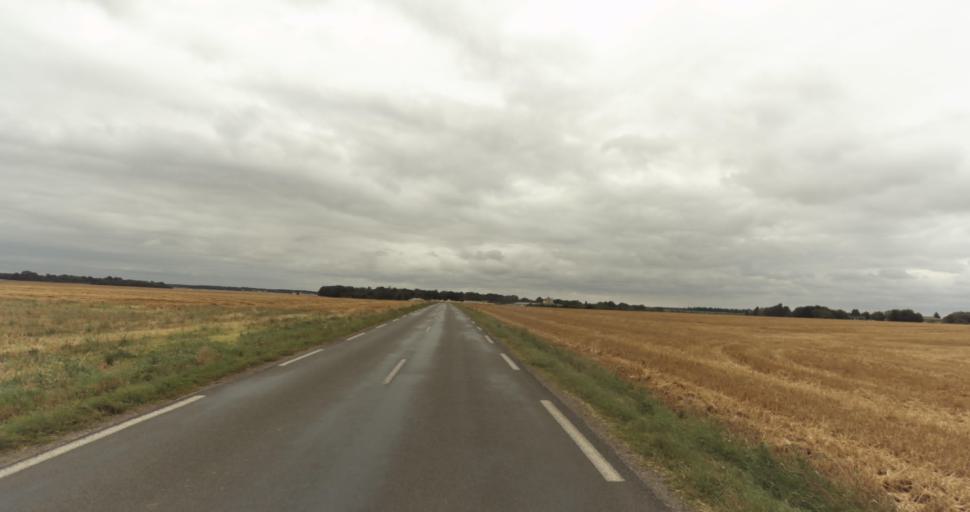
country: FR
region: Haute-Normandie
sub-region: Departement de l'Eure
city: Gravigny
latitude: 49.0267
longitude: 1.2417
